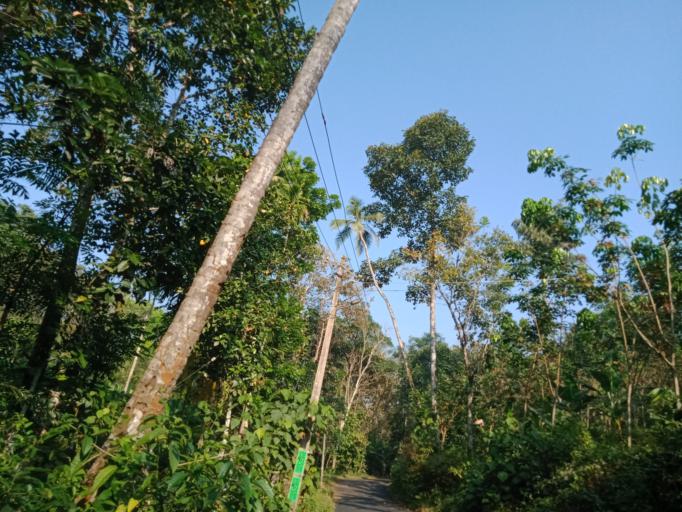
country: IN
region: Kerala
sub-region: Kottayam
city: Lalam
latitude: 9.5994
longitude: 76.7016
